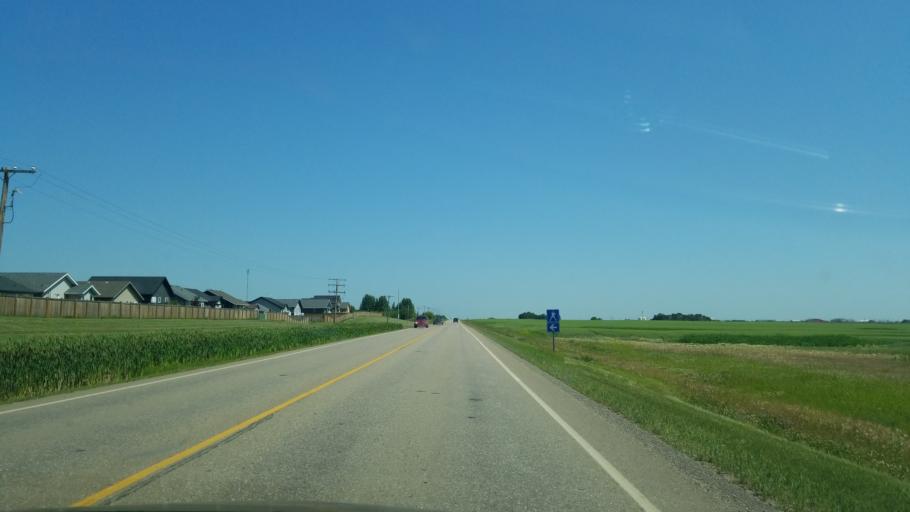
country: CA
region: Saskatchewan
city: Lloydminster
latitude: 53.2489
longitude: -109.9993
